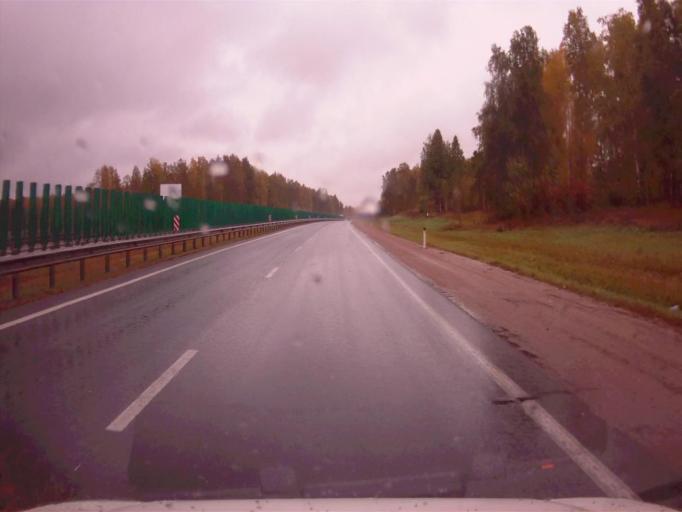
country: RU
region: Chelyabinsk
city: Dolgoderevenskoye
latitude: 55.3326
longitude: 61.3165
